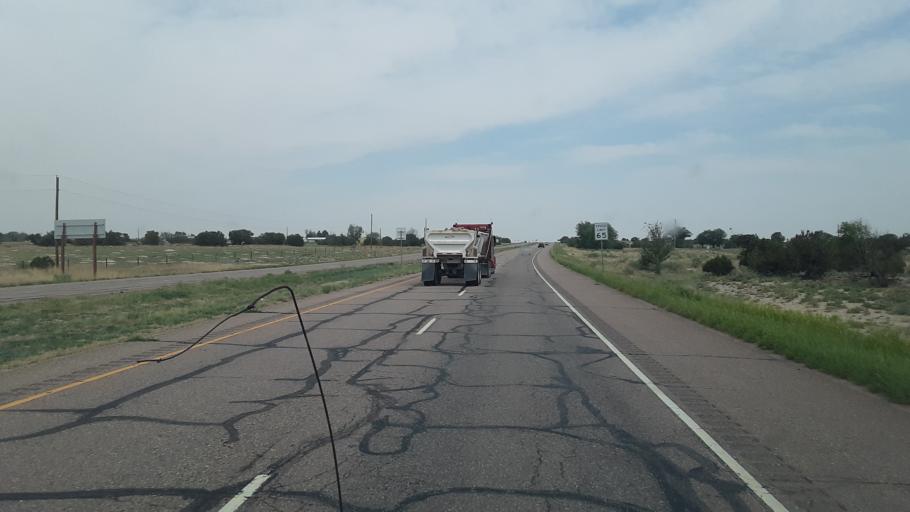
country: US
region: Colorado
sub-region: Fremont County
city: Penrose
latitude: 38.4157
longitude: -105.0310
